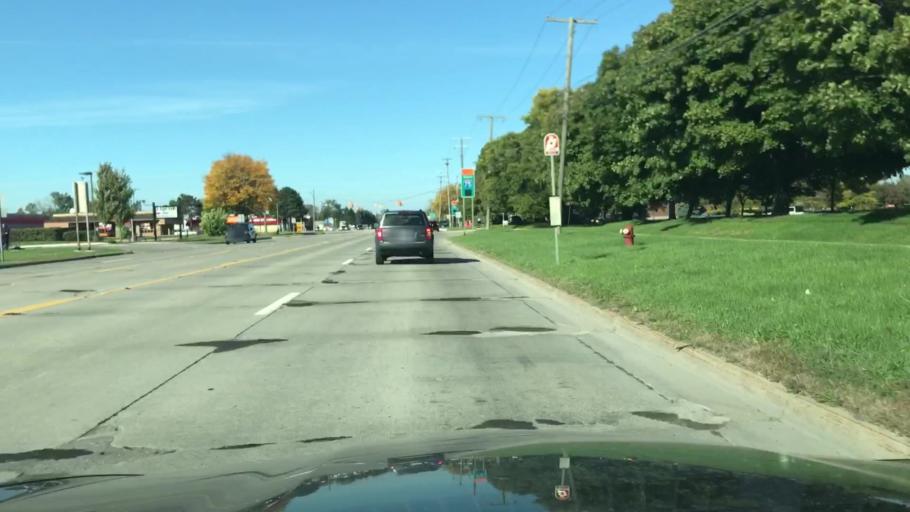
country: US
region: Michigan
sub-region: Macomb County
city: Sterling Heights
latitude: 42.5619
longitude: -83.0886
